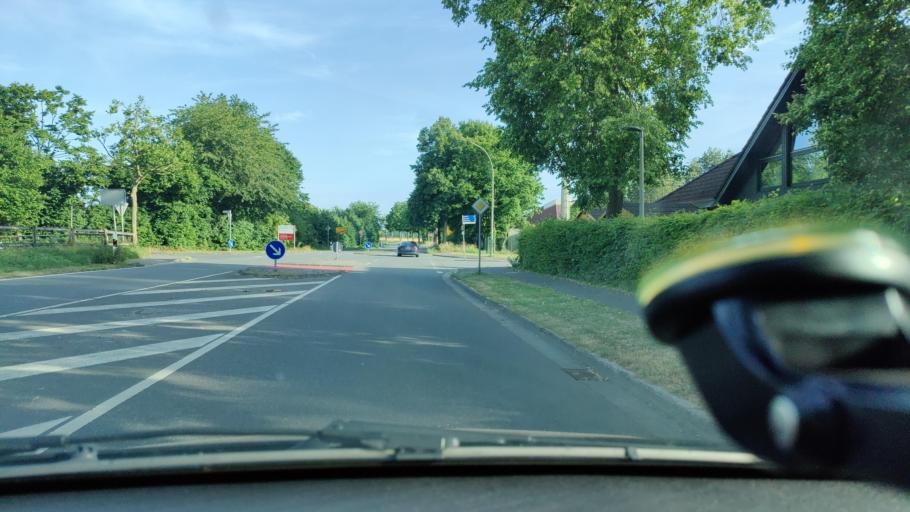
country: DE
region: North Rhine-Westphalia
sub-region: Regierungsbezirk Munster
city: Schoppingen
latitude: 52.0173
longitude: 7.2155
